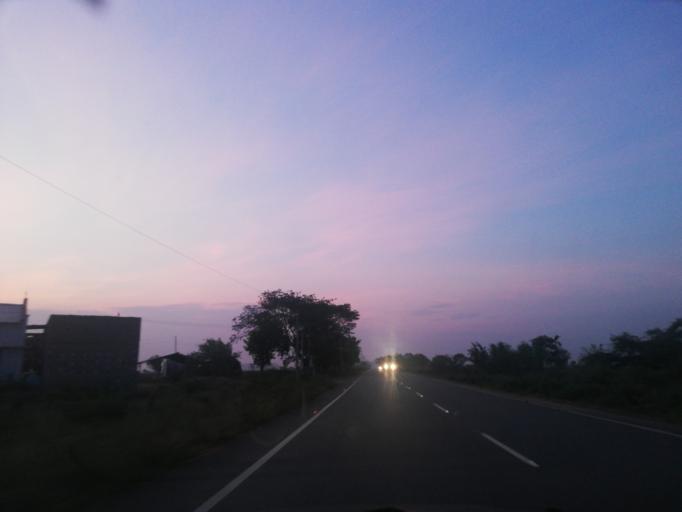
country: IN
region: Andhra Pradesh
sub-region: Guntur
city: Macherla
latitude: 16.6935
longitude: 79.2471
